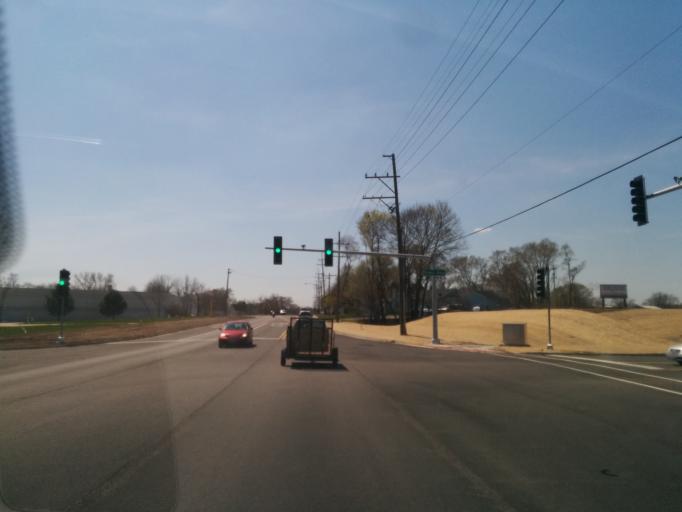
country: US
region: Illinois
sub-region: Kane County
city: South Elgin
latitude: 42.0101
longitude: -88.2900
